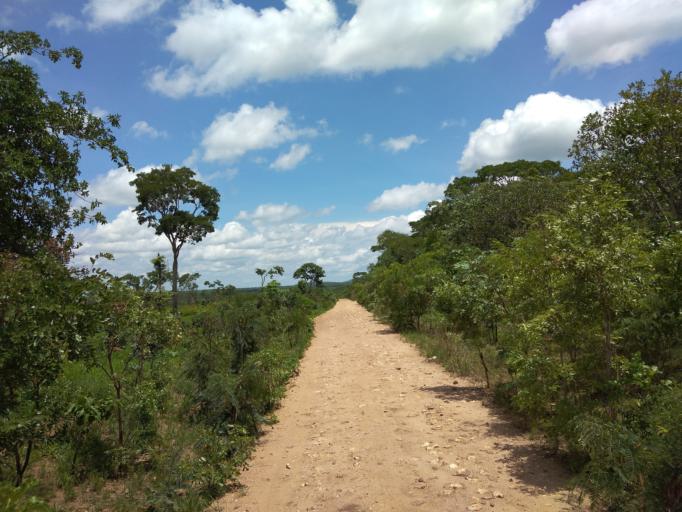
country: ZM
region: Central
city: Mkushi
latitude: -13.9577
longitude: 29.8934
